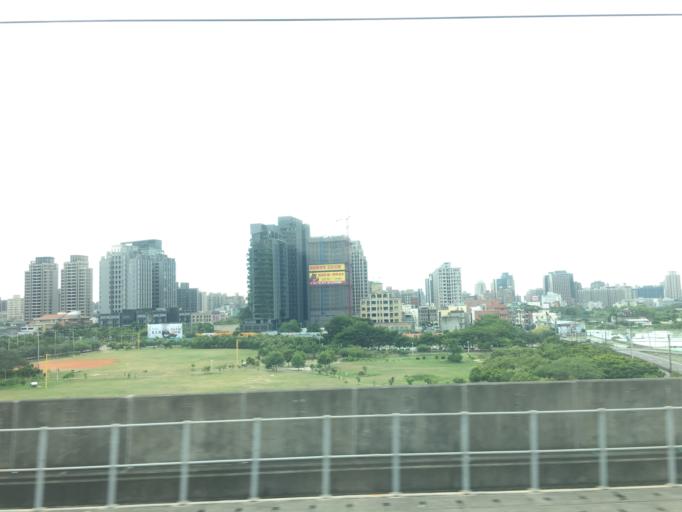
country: TW
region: Taiwan
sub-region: Hsinchu
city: Zhubei
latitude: 24.8120
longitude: 121.0411
